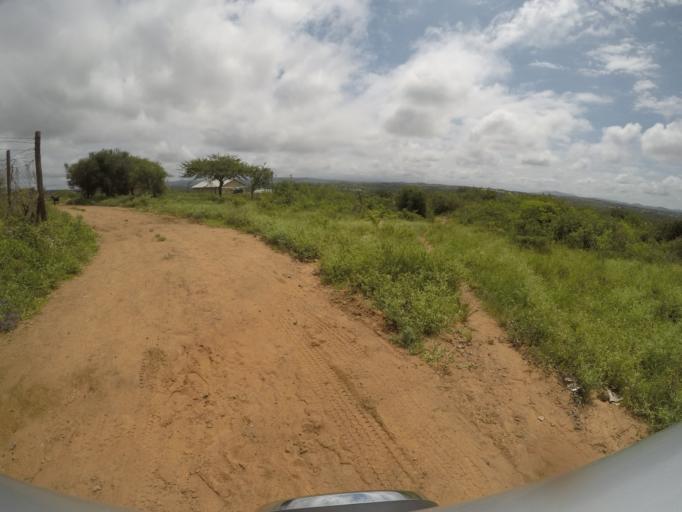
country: ZA
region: KwaZulu-Natal
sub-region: uThungulu District Municipality
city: Empangeni
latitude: -28.5755
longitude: 31.8438
